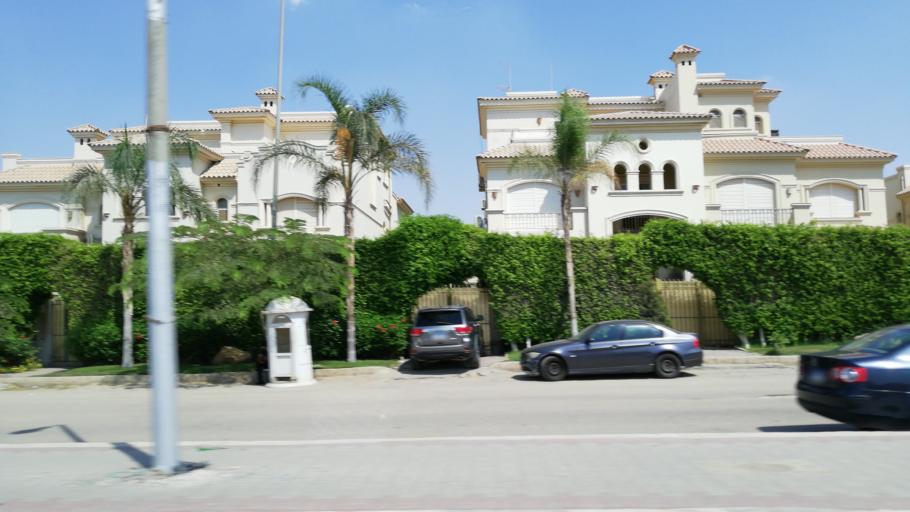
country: EG
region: Muhafazat al Qalyubiyah
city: Al Khankah
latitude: 30.0537
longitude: 31.4752
